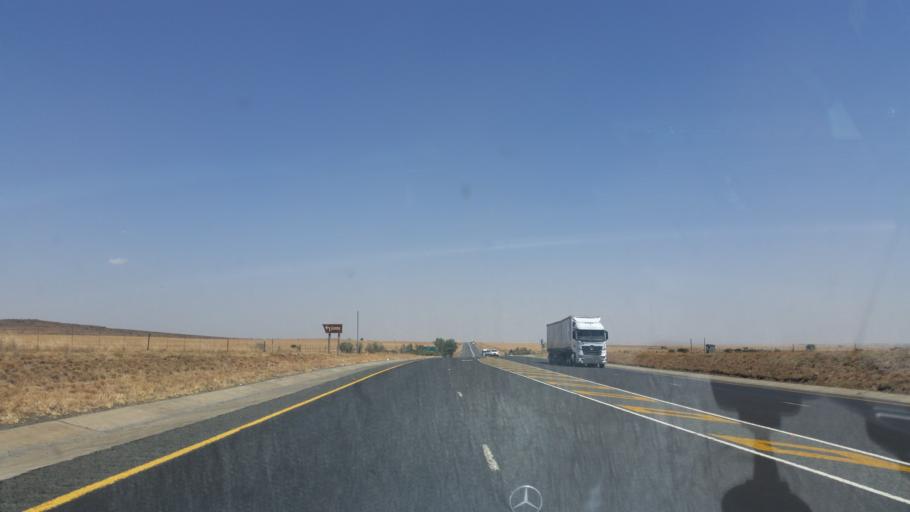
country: ZA
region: Orange Free State
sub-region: Lejweleputswa District Municipality
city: Brandfort
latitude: -28.8138
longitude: 26.6708
